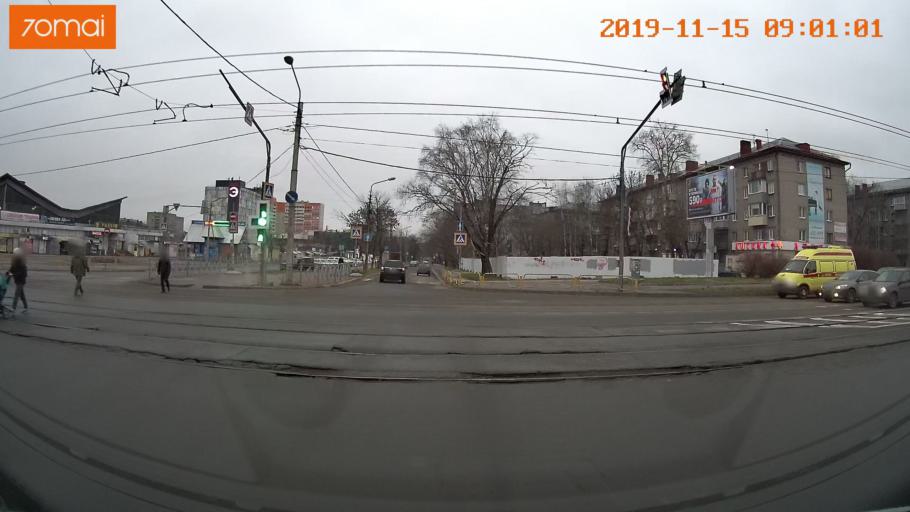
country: RU
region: Vologda
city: Cherepovets
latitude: 59.1303
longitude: 37.9250
